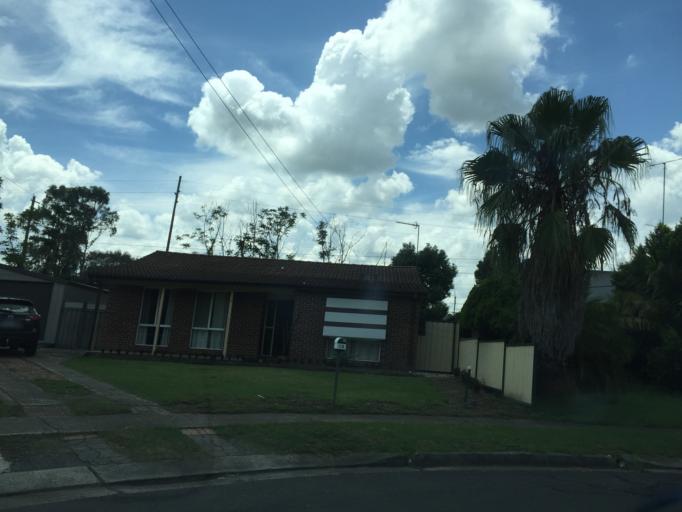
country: AU
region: New South Wales
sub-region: Blacktown
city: Riverstone
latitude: -33.6985
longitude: 150.8702
